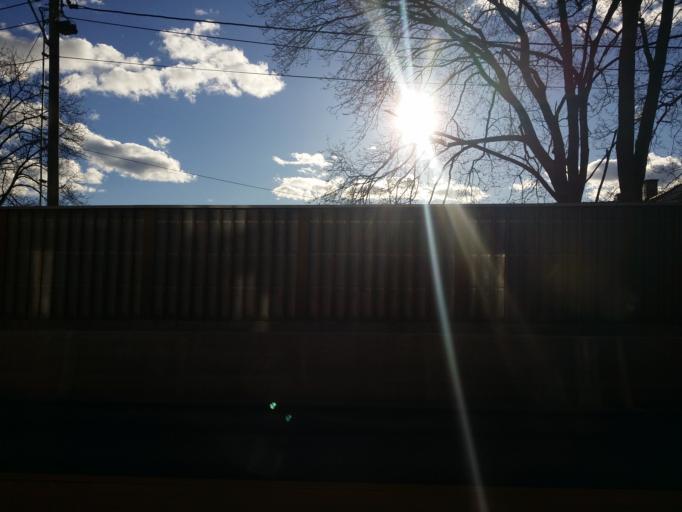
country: NO
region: Akershus
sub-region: Oppegard
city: Kolbotn
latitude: 59.8663
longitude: 10.7834
